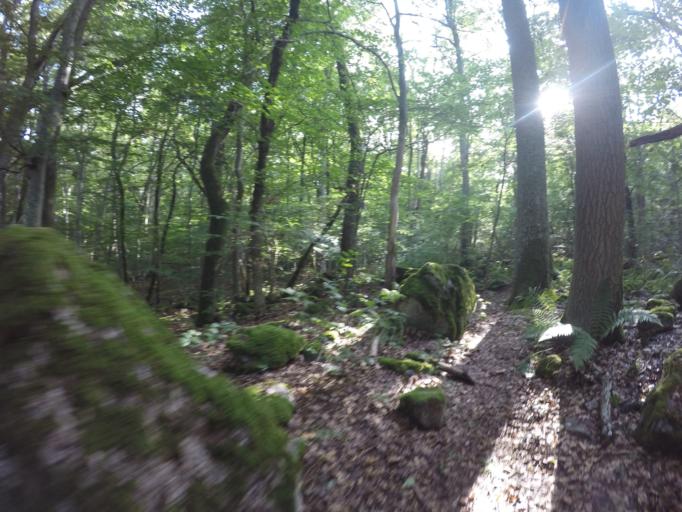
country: SE
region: Soedermanland
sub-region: Eskilstuna Kommun
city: Kvicksund
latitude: 59.4805
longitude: 16.2932
